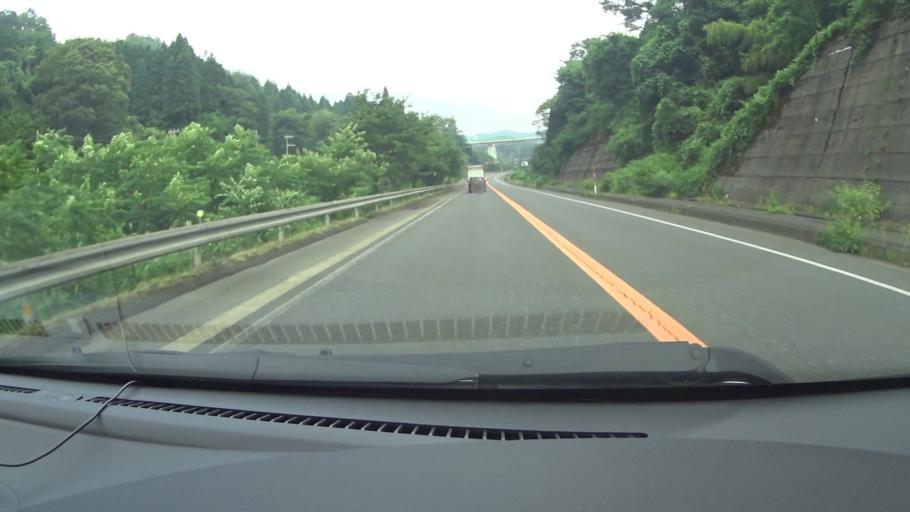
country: JP
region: Kyoto
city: Maizuru
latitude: 35.3762
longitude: 135.3197
